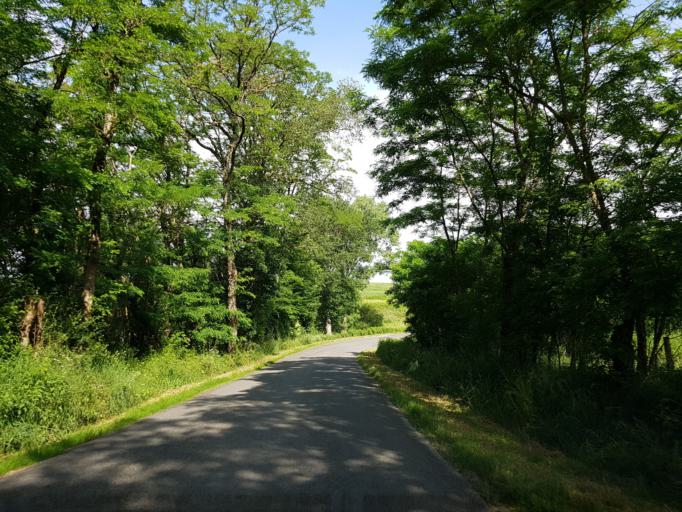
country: FR
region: Poitou-Charentes
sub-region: Departement de la Charente
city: Exideuil
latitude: 45.8899
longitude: 0.6951
